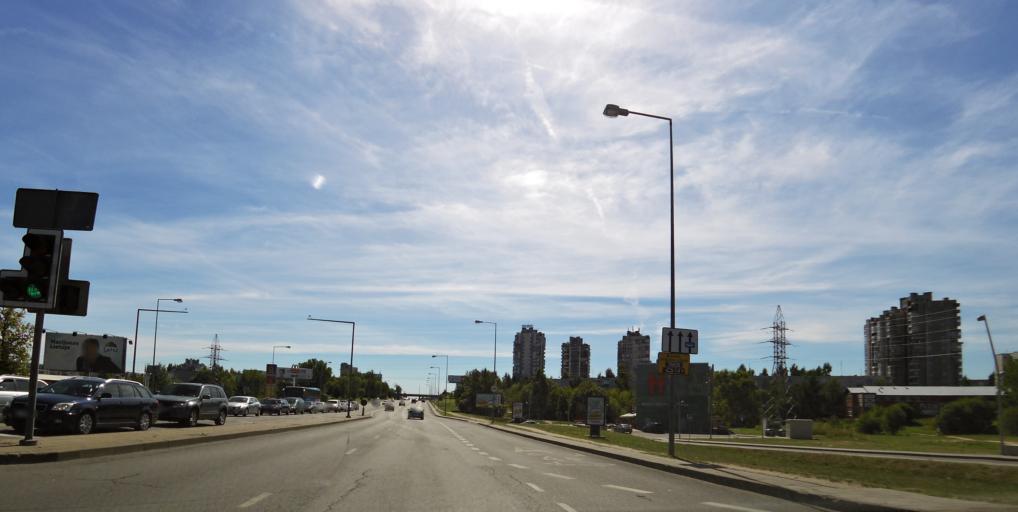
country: LT
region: Vilnius County
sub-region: Vilnius
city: Fabijoniskes
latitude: 54.7211
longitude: 25.2441
